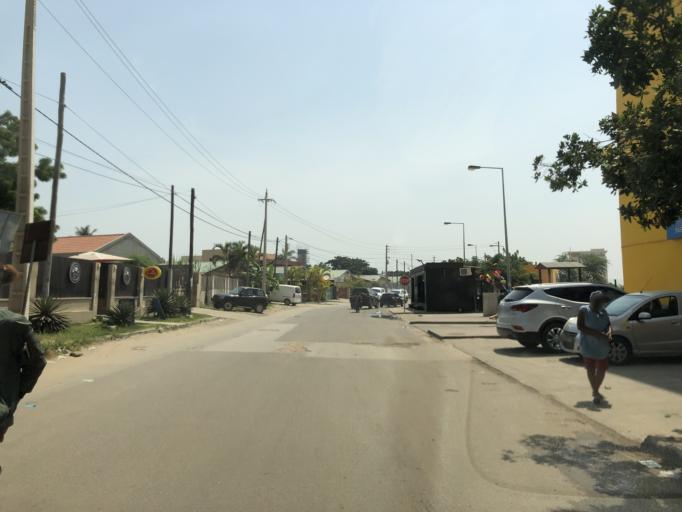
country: AO
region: Luanda
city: Luanda
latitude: -8.9058
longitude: 13.2340
